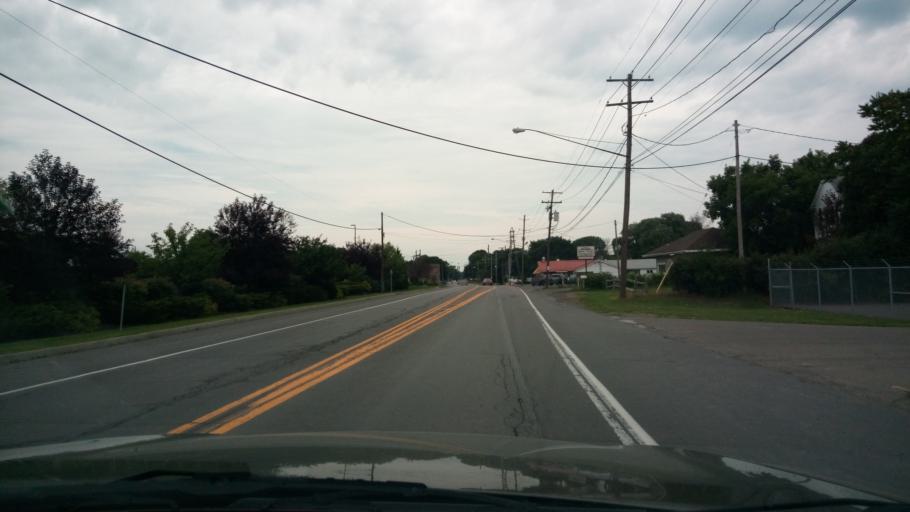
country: US
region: New York
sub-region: Chemung County
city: Elmira Heights
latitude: 42.1292
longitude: -76.8110
